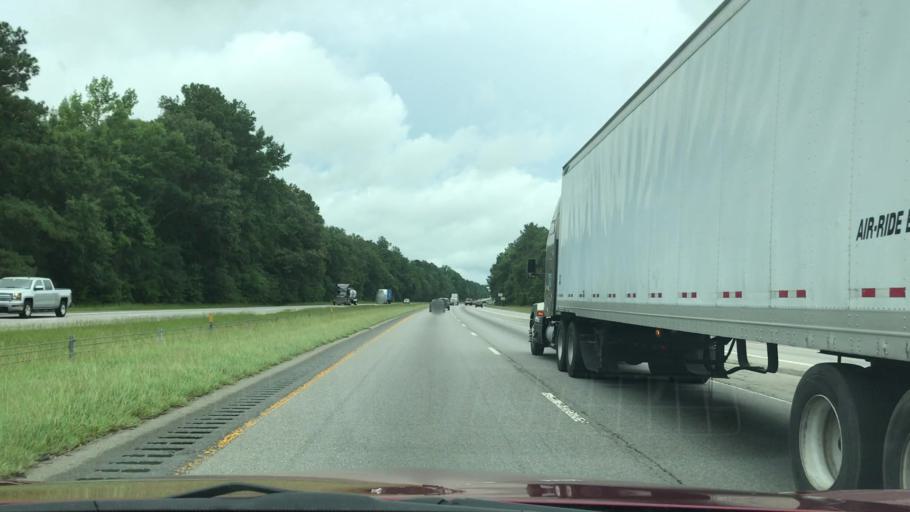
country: US
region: South Carolina
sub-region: Orangeburg County
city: Brookdale
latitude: 33.4989
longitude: -80.7687
